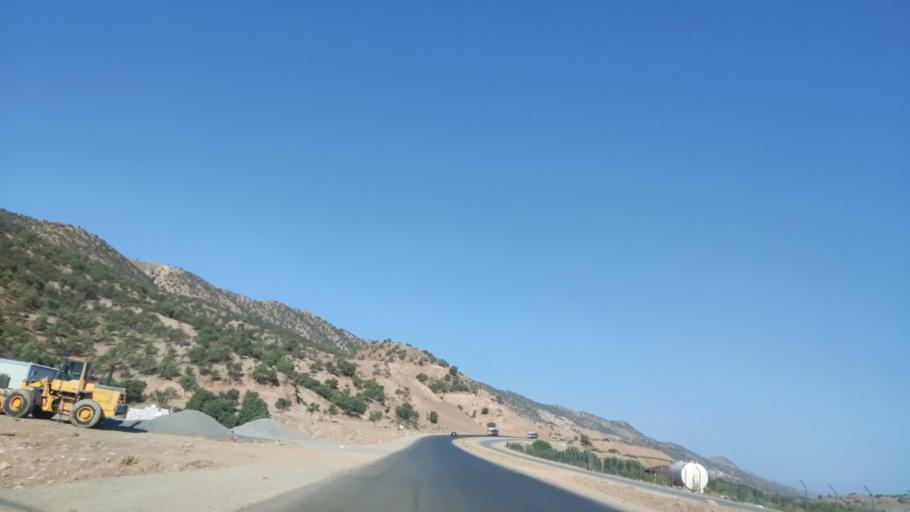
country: IQ
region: Arbil
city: Shaqlawah
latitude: 36.4310
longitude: 44.3171
